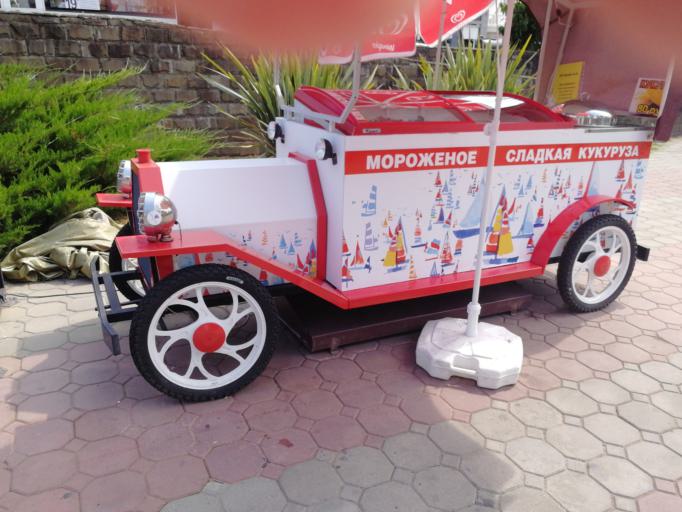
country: RU
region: Krasnodarskiy
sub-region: Sochi City
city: Sochi
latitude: 43.5910
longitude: 39.7266
